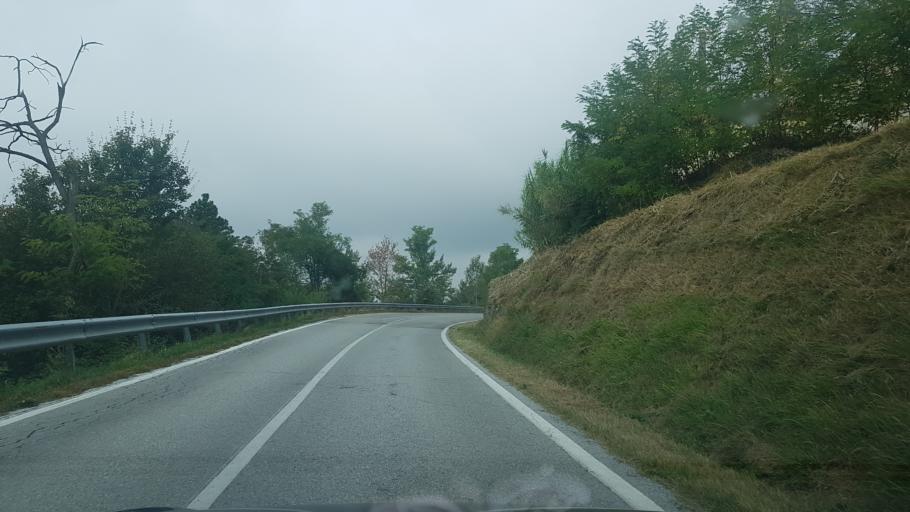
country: IT
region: Piedmont
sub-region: Provincia di Cuneo
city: Sale delle Langhe
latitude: 44.4049
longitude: 8.1106
